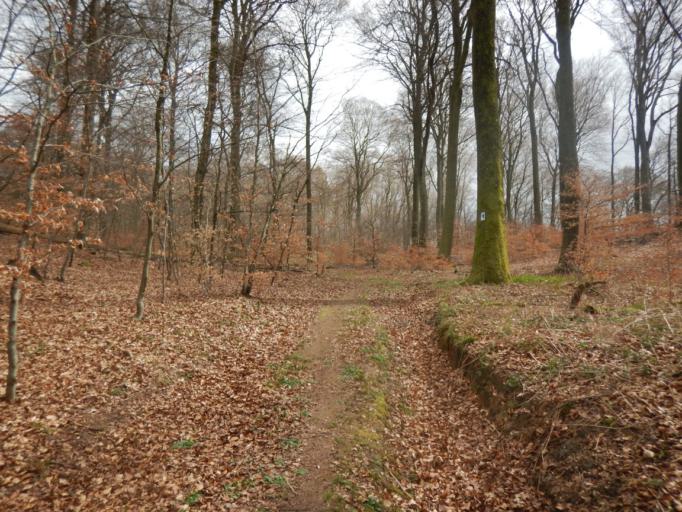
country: LU
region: Luxembourg
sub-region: Canton de Mersch
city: Lorentzweiler
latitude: 49.7083
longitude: 6.1649
